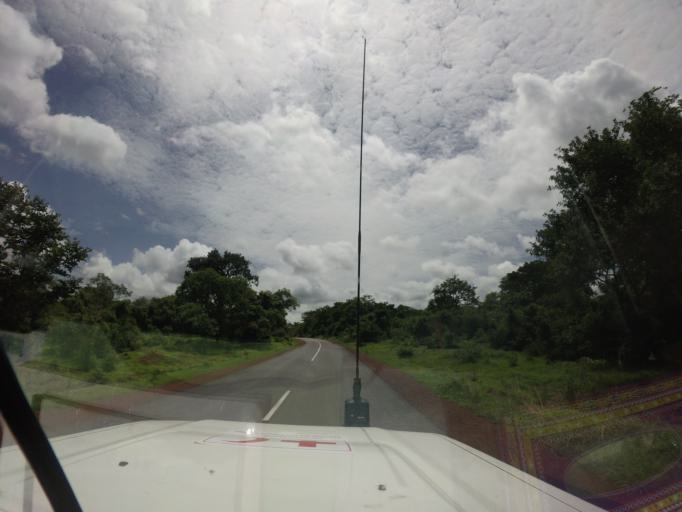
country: SL
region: Northern Province
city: Gberia Fotombu
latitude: 10.1050
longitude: -11.1501
